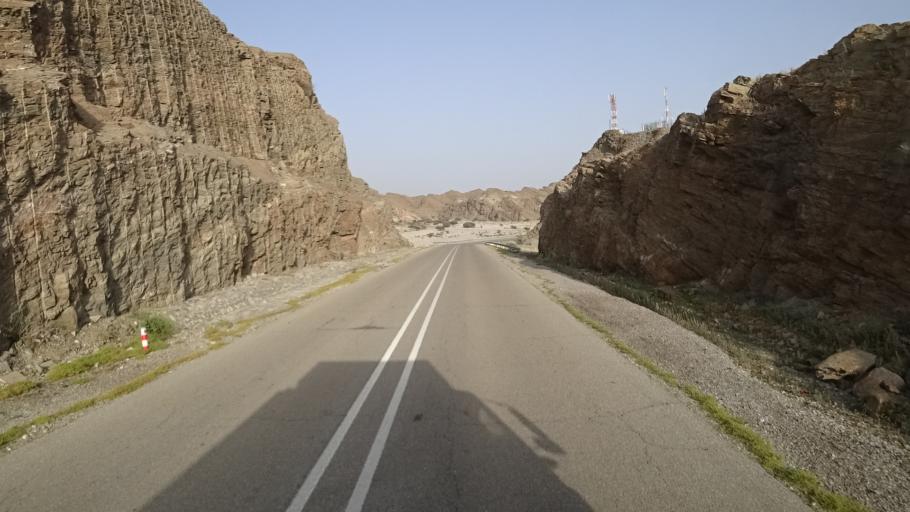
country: OM
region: Muhafazat Masqat
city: Bawshar
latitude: 23.3578
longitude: 58.5305
